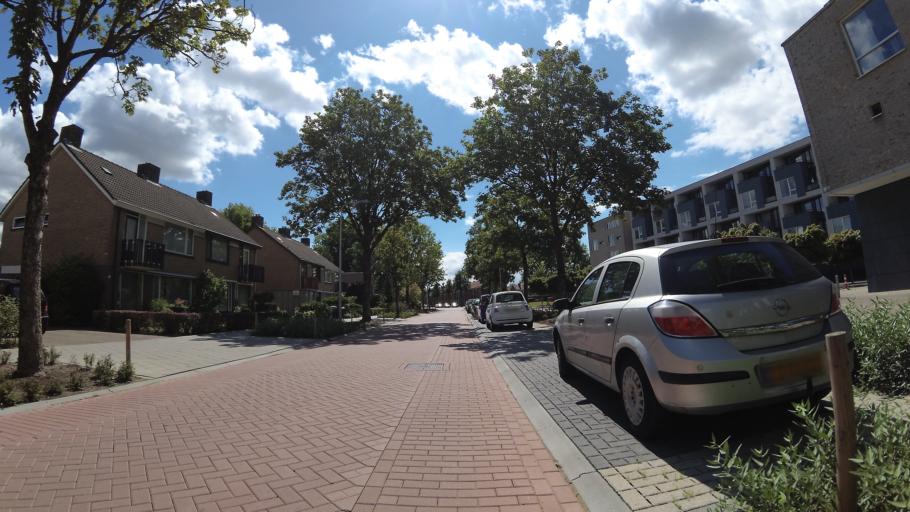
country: NL
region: North Brabant
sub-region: Gemeente Goirle
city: Goirle
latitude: 51.5540
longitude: 5.0511
